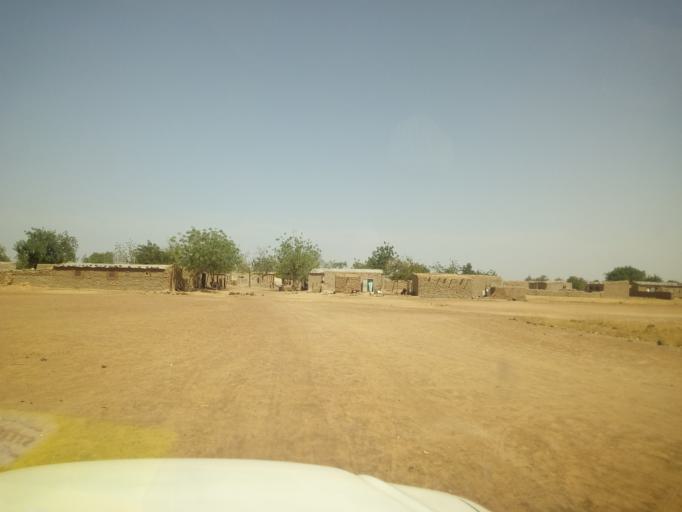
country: ML
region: Koulikoro
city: Koulikoro
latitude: 12.6479
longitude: -7.7096
